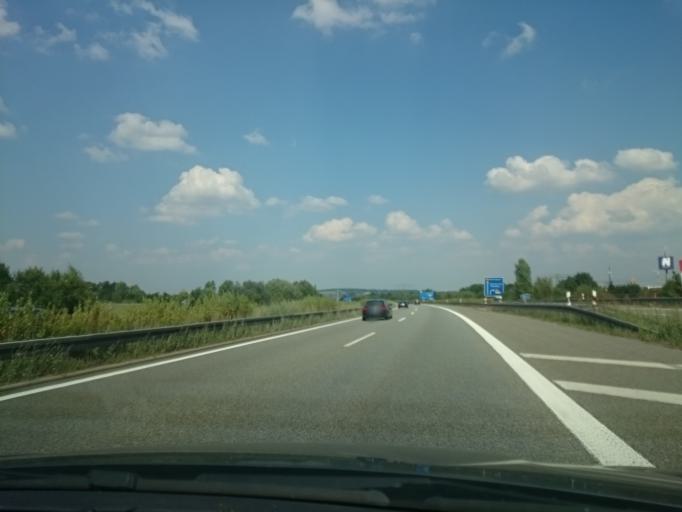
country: DE
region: Saxony
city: Neukirchen
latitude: 50.8035
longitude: 12.8581
